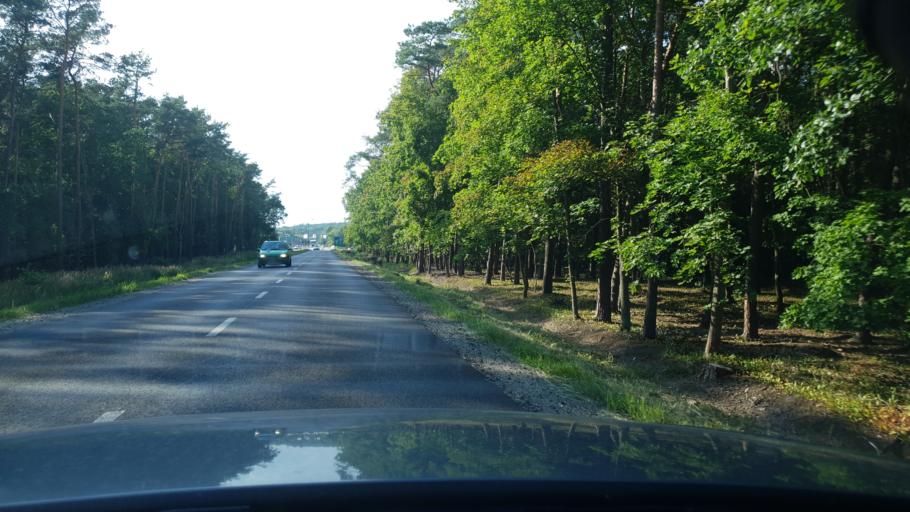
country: PL
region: Kujawsko-Pomorskie
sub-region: Grudziadz
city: Grudziadz
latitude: 53.4484
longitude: 18.7394
